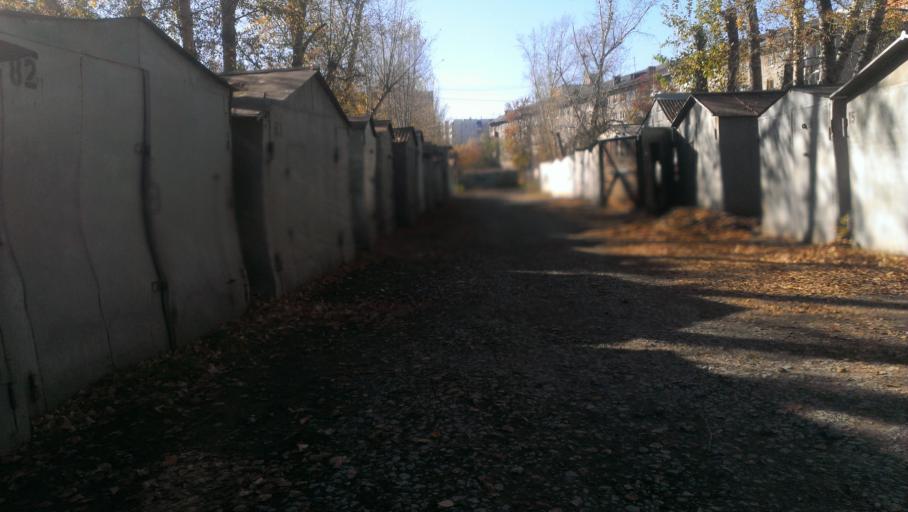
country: RU
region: Altai Krai
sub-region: Gorod Barnaulskiy
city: Barnaul
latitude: 53.3639
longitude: 83.6836
